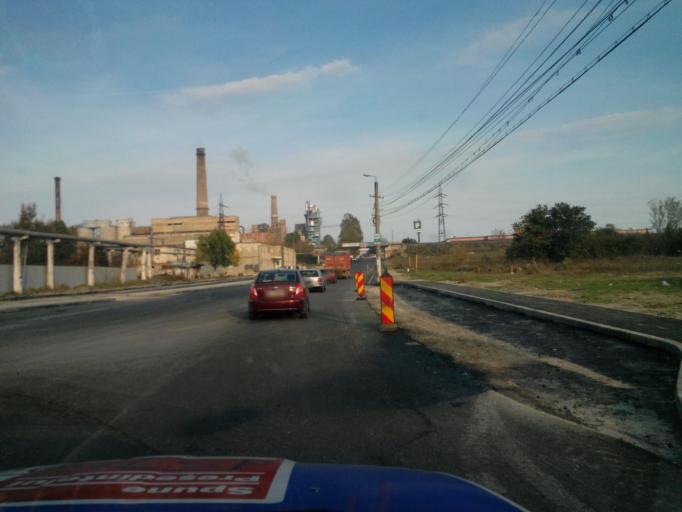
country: RO
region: Tulcea
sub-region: Municipiul Tulcea
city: Tulcea
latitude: 45.1775
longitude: 28.7612
